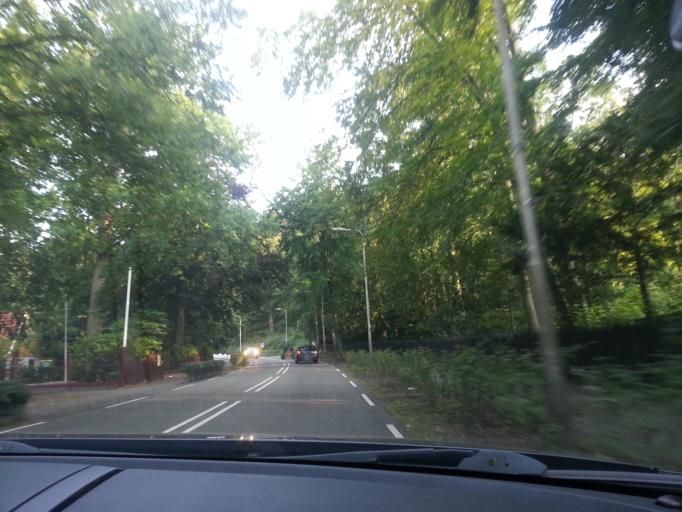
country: NL
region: South Holland
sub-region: Gemeente Lisse
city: Lisse
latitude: 52.2685
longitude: 4.5427
